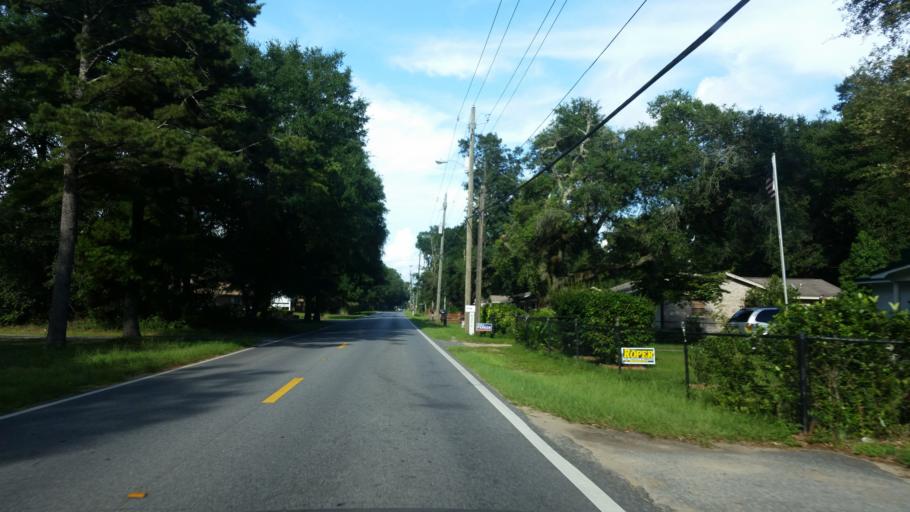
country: US
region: Florida
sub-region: Santa Rosa County
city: Milton
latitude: 30.6216
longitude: -87.0617
